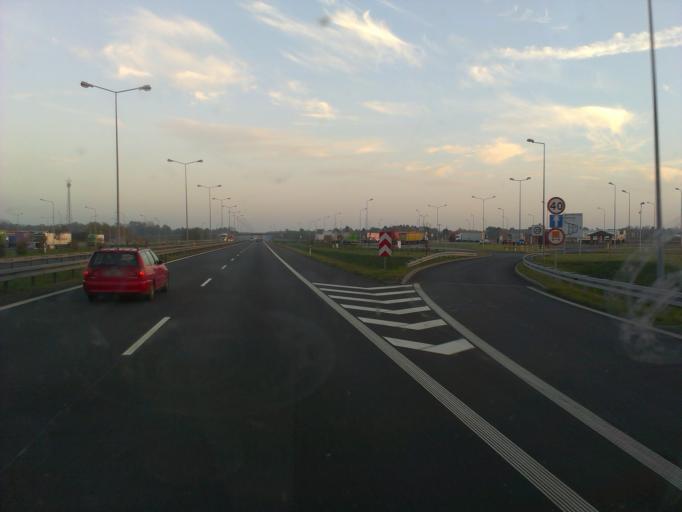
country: PL
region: Opole Voivodeship
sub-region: Powiat opolski
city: Proszkow
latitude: 50.5703
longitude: 17.8587
